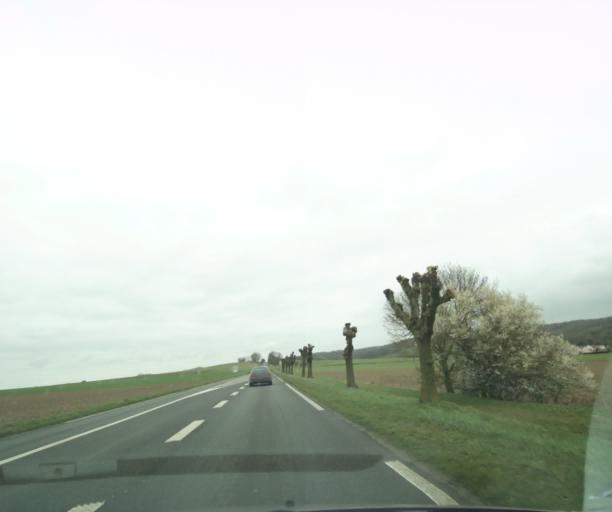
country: FR
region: Picardie
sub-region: Departement de l'Oise
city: Noyon
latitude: 49.5985
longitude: 3.0090
